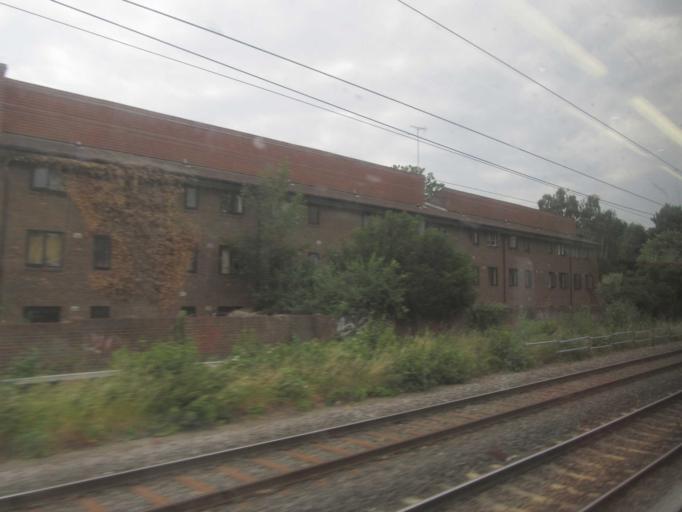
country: GB
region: England
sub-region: Greater London
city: Belsize Park
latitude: 51.5495
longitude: -0.2000
